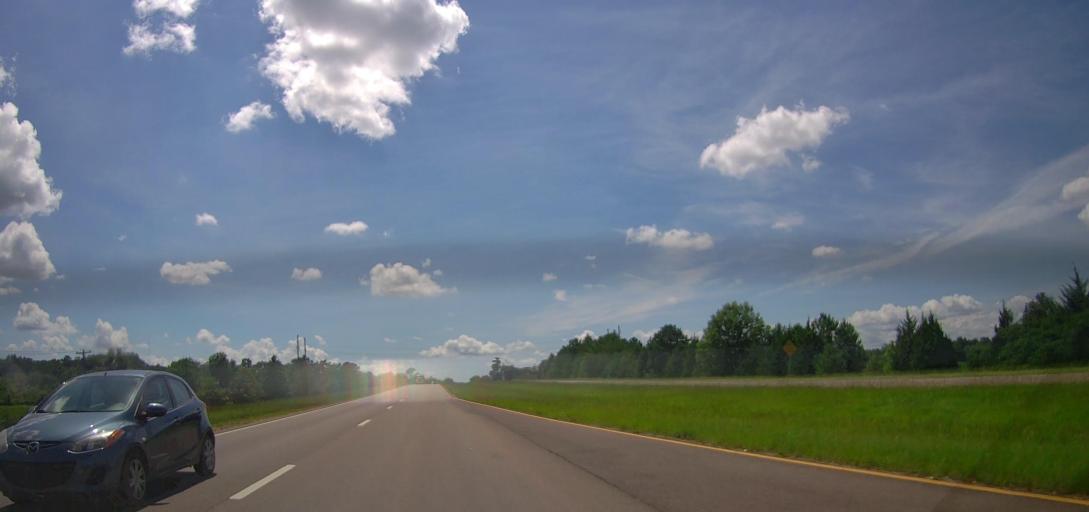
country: US
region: Mississippi
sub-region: Monroe County
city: Aberdeen
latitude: 33.8157
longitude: -88.5345
